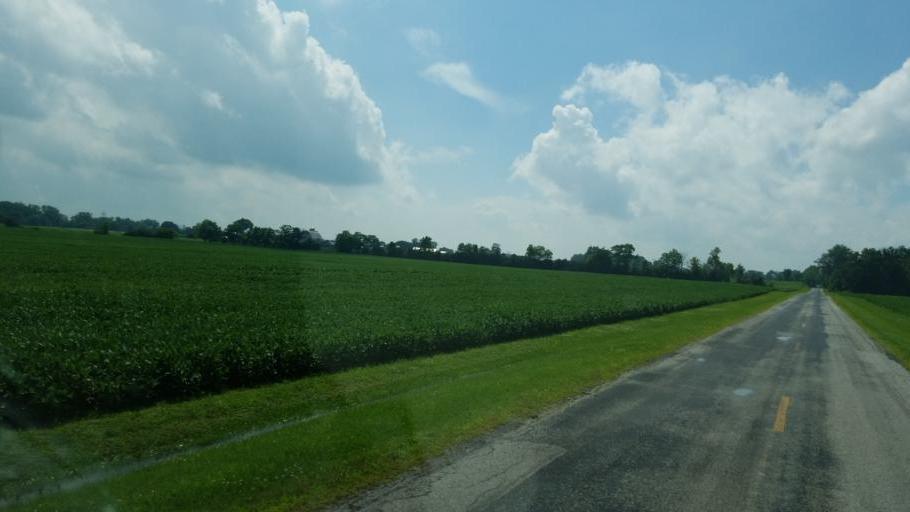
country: US
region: Ohio
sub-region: Union County
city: Richwood
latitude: 40.5657
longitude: -83.3760
